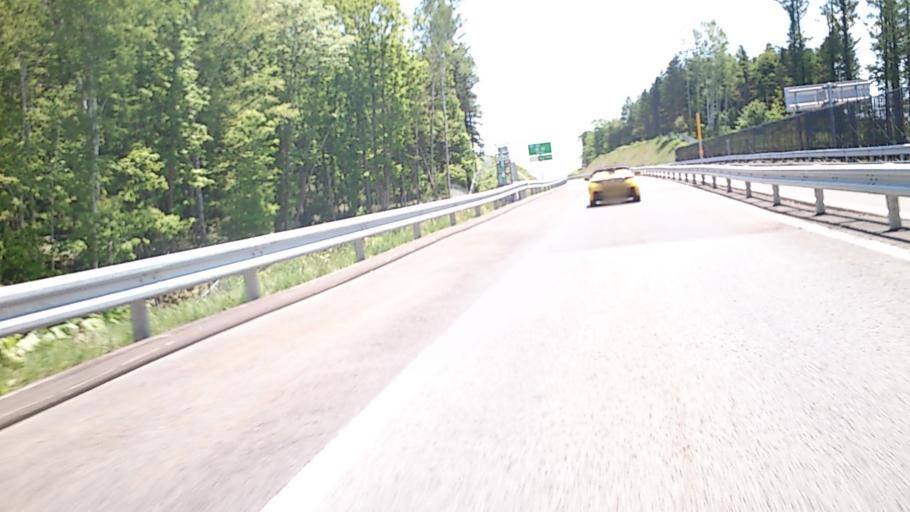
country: JP
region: Hokkaido
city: Nayoro
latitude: 44.4861
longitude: 142.3626
